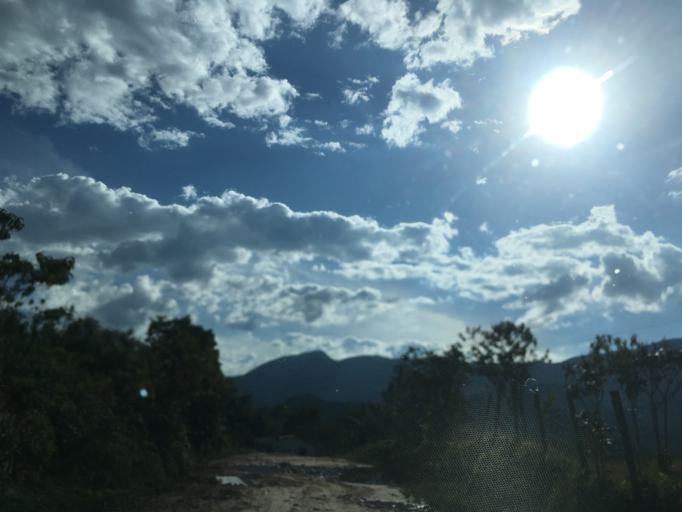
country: CO
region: Santander
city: Oiba
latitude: 6.0990
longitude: -73.1964
